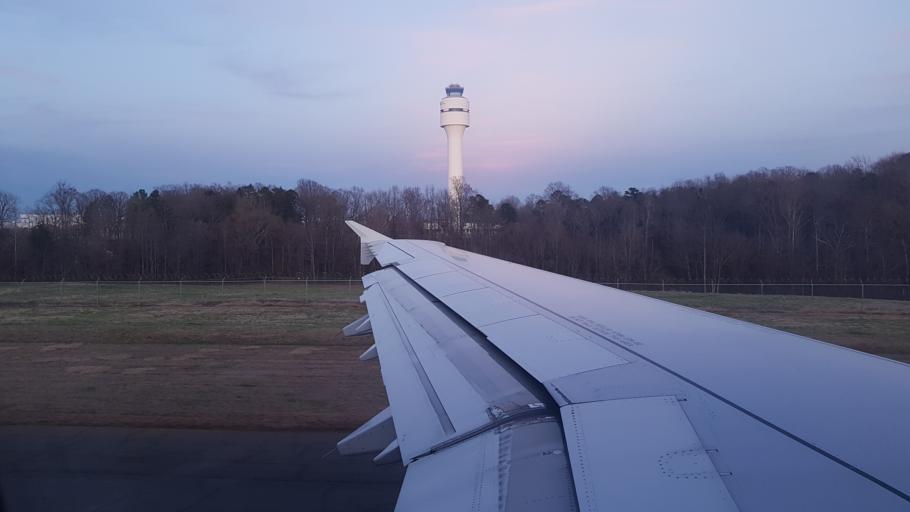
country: US
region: North Carolina
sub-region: Gaston County
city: Belmont
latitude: 35.2031
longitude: -80.9490
